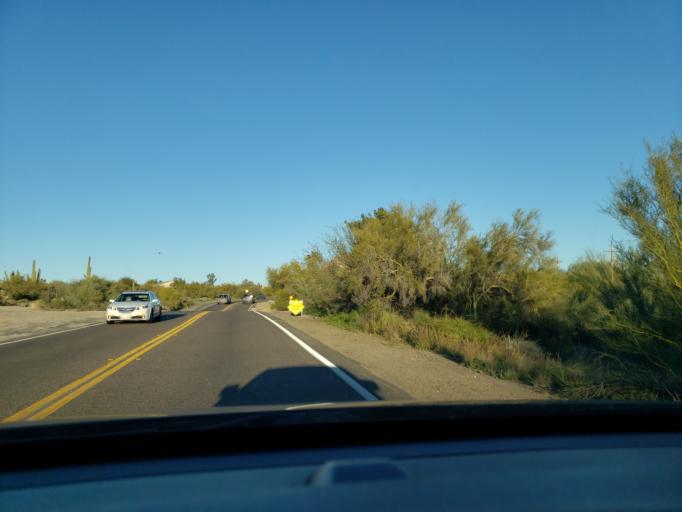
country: US
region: Arizona
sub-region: Maricopa County
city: Carefree
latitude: 33.7996
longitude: -111.9361
